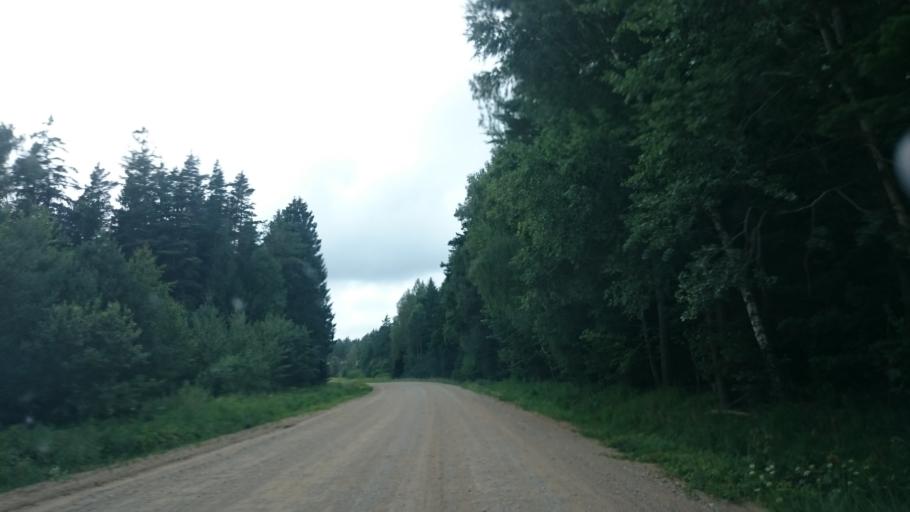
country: LV
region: Pavilostas
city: Pavilosta
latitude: 56.8569
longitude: 21.2343
